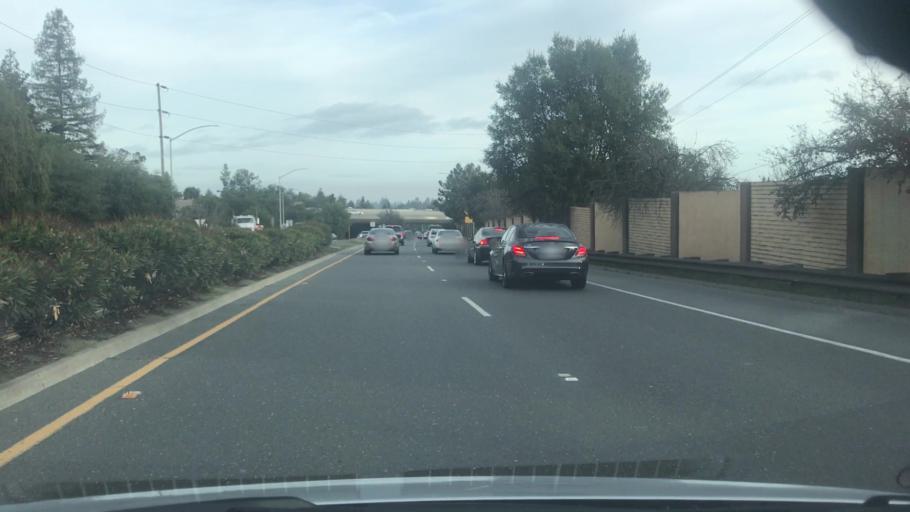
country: US
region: California
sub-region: Santa Clara County
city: Loyola
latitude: 37.3321
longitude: -122.0689
